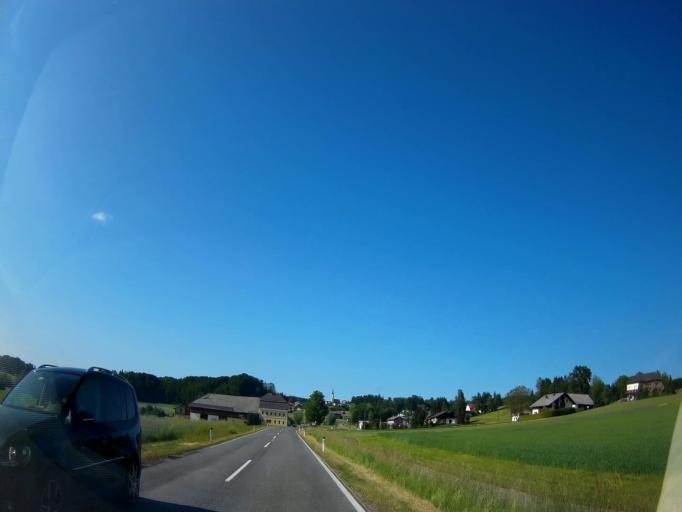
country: AT
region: Salzburg
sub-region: Politischer Bezirk Salzburg-Umgebung
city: Dorfbeuern
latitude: 48.0613
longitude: 12.9875
